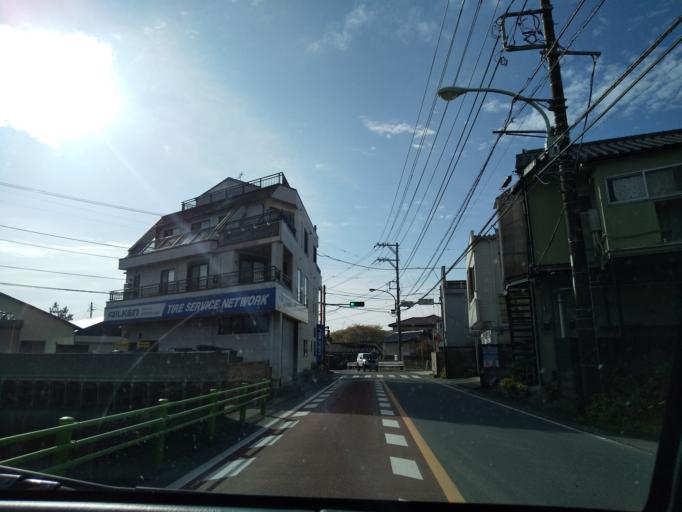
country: JP
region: Tokyo
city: Itsukaichi
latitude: 35.6793
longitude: 139.2625
